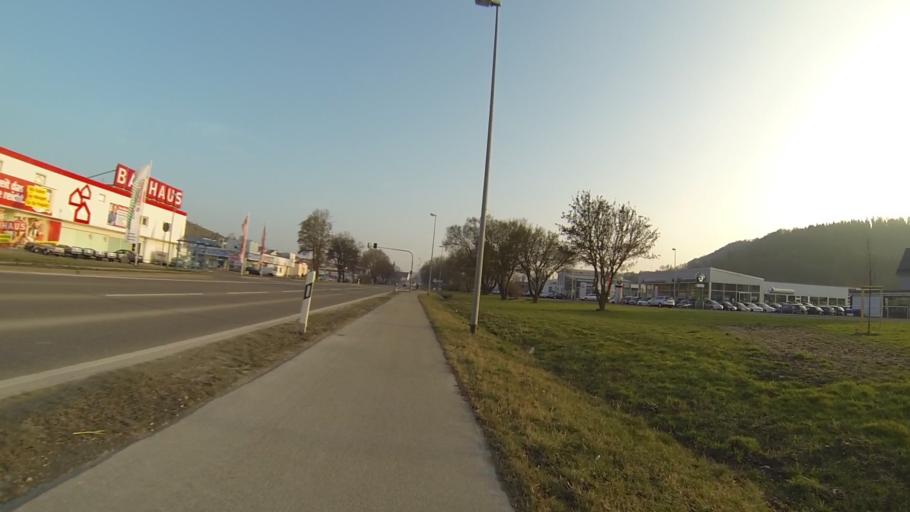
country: DE
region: Baden-Wuerttemberg
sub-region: Regierungsbezirk Stuttgart
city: Heidenheim an der Brenz
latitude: 48.7152
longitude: 10.1593
